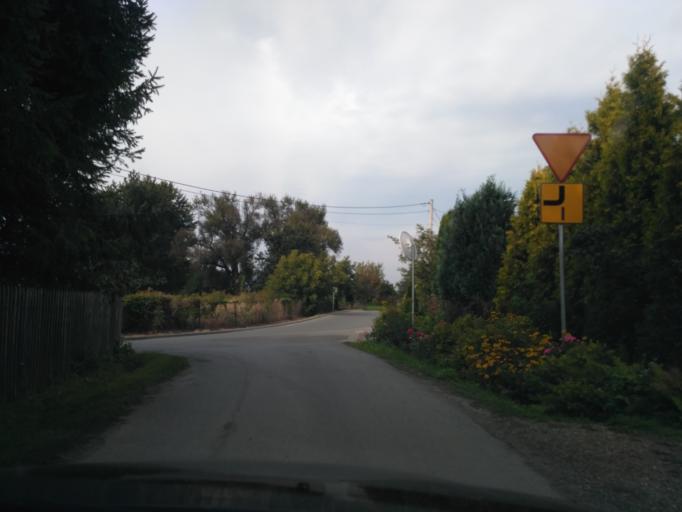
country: PL
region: Subcarpathian Voivodeship
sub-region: Powiat rzeszowski
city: Swilcza
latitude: 50.0798
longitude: 21.9025
